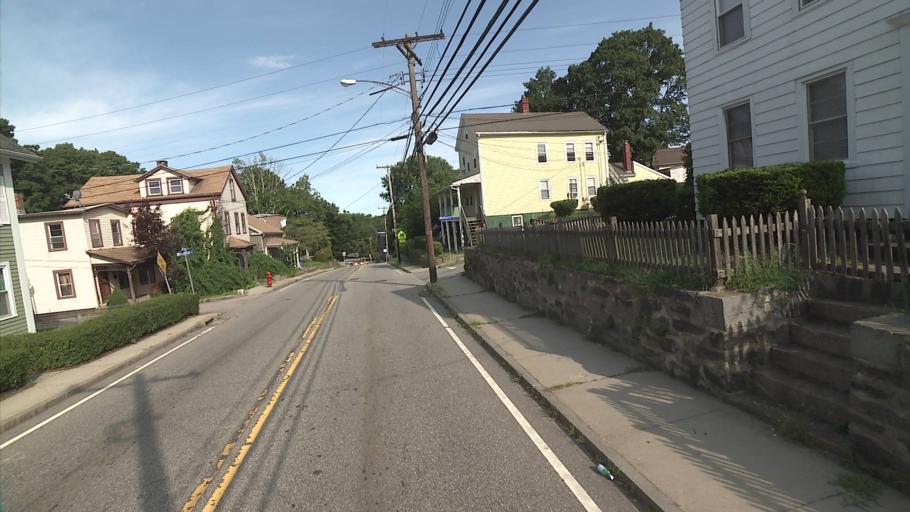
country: US
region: Connecticut
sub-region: New London County
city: Norwich
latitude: 41.5216
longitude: -72.0605
